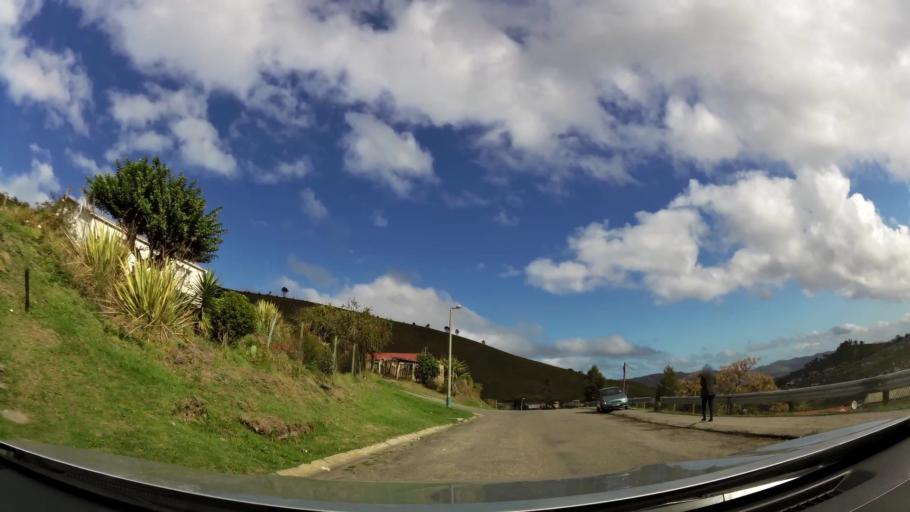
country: ZA
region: Western Cape
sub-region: Eden District Municipality
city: Knysna
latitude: -34.0538
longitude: 23.1048
